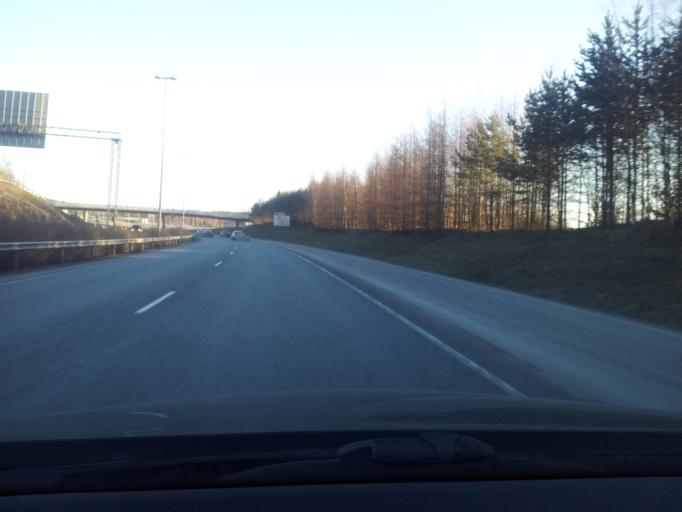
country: FI
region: Uusimaa
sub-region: Helsinki
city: Kauniainen
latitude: 60.1952
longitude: 24.7433
